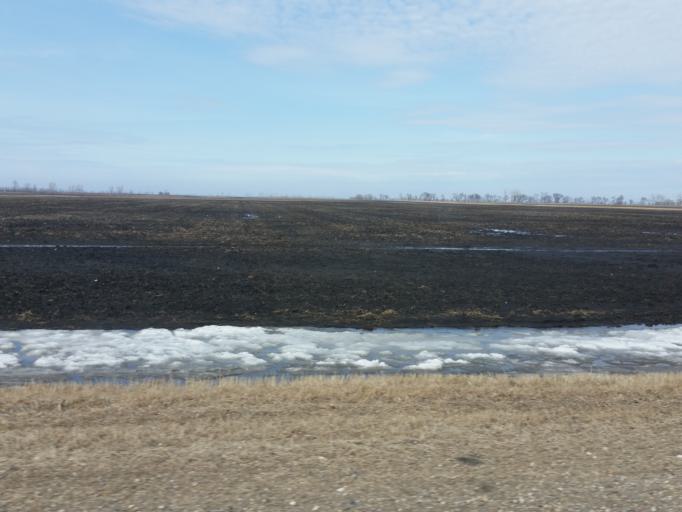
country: US
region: North Dakota
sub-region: Walsh County
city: Grafton
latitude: 48.4265
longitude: -97.2363
